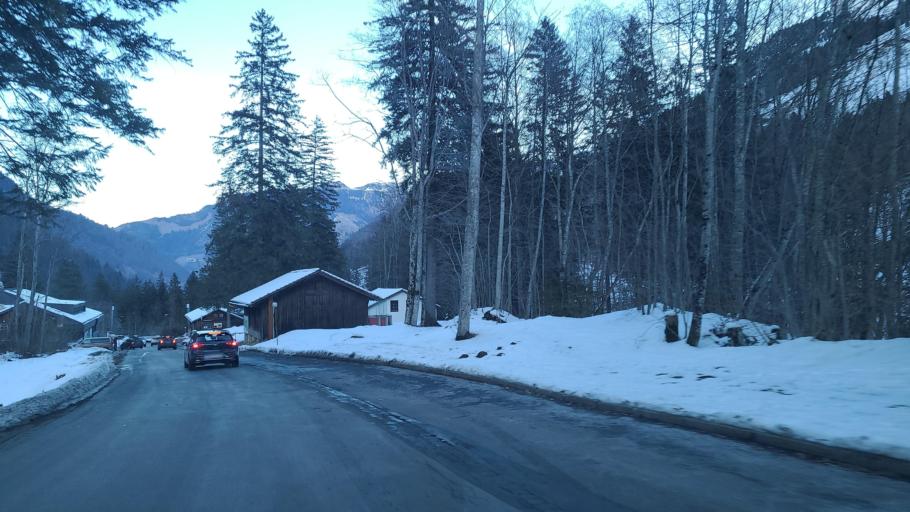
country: CH
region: Obwalden
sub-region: Obwalden
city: Sachseln
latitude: 46.8137
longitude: 8.2829
